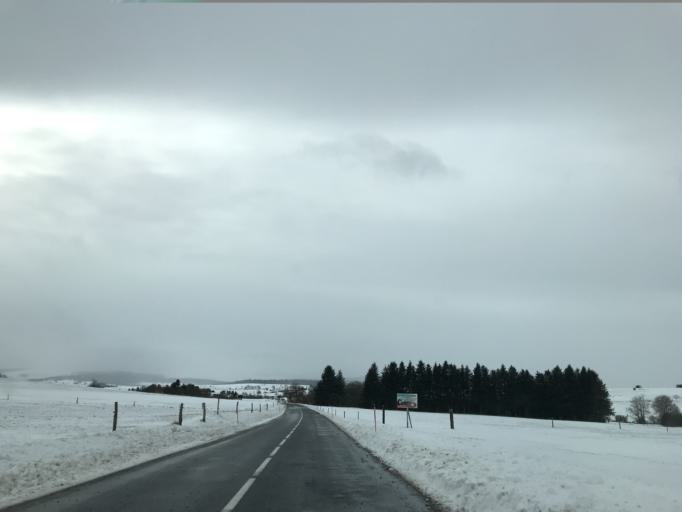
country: FR
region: Auvergne
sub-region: Departement du Puy-de-Dome
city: Aydat
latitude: 45.6651
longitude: 2.9323
